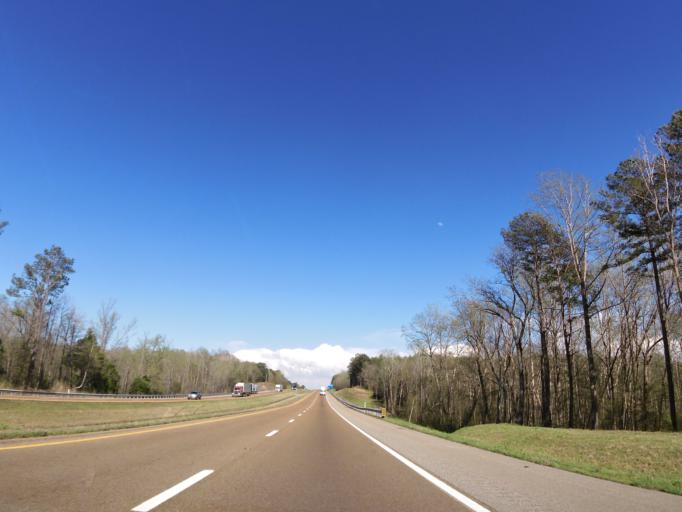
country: US
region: Tennessee
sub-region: Decatur County
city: Parsons
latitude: 35.8233
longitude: -88.1280
